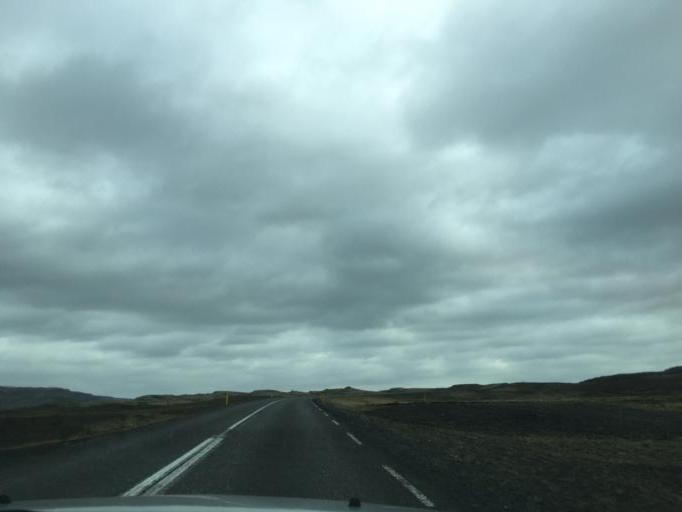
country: IS
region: South
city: Vestmannaeyjar
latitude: 64.2499
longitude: -20.2048
